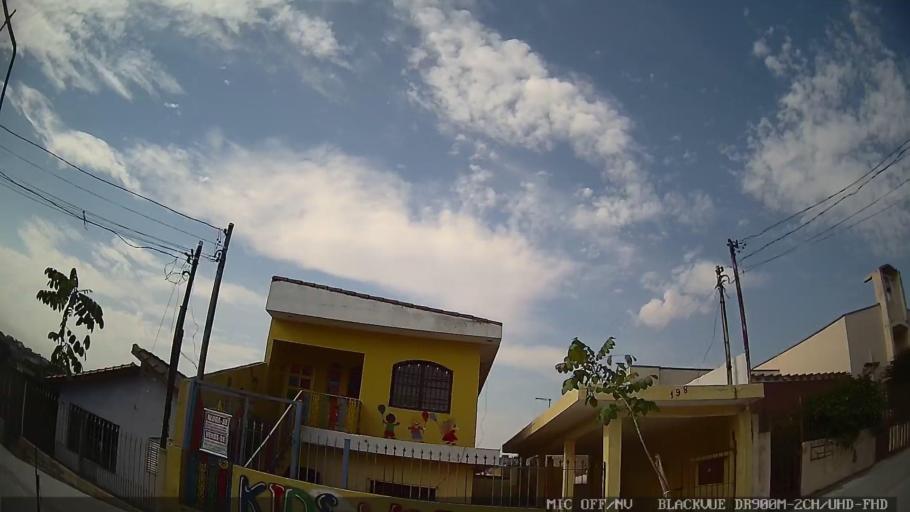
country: BR
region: Sao Paulo
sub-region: Ferraz De Vasconcelos
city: Ferraz de Vasconcelos
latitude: -23.5391
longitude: -46.4100
